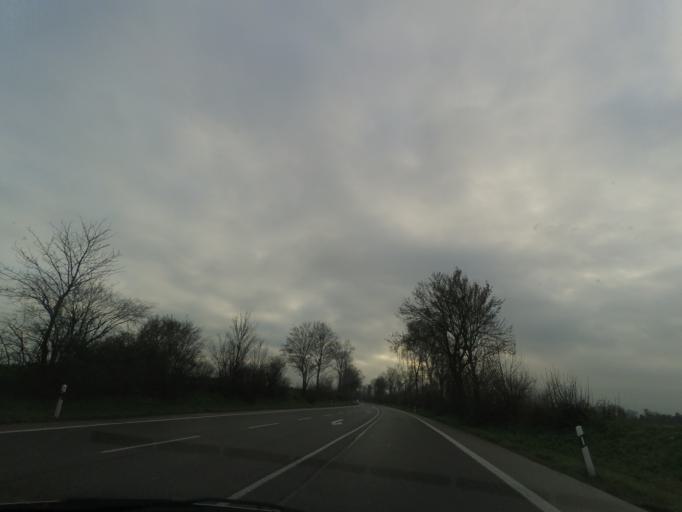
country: DE
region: North Rhine-Westphalia
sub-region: Regierungsbezirk Dusseldorf
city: Neubrueck
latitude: 51.1515
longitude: 6.5948
